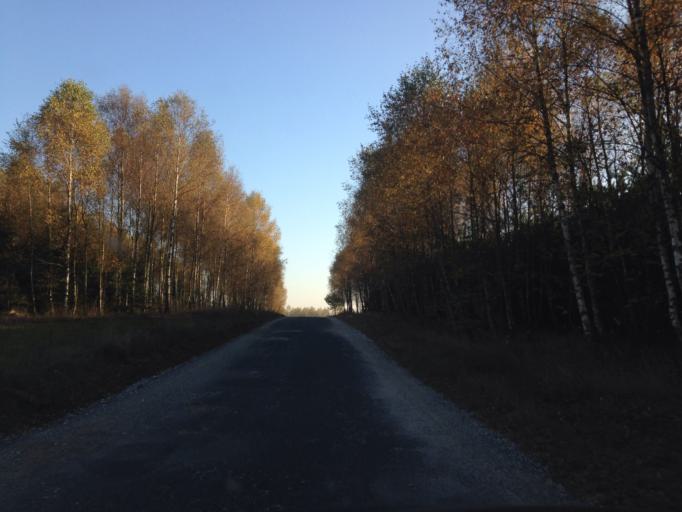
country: PL
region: Kujawsko-Pomorskie
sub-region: Powiat brodnicki
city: Gorzno
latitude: 53.1686
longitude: 19.6410
